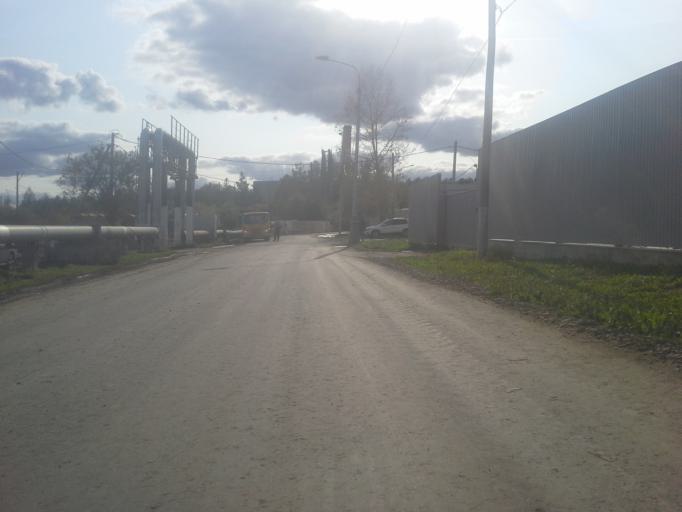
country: RU
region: Moskovskaya
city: Kievskij
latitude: 55.4272
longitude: 36.8684
